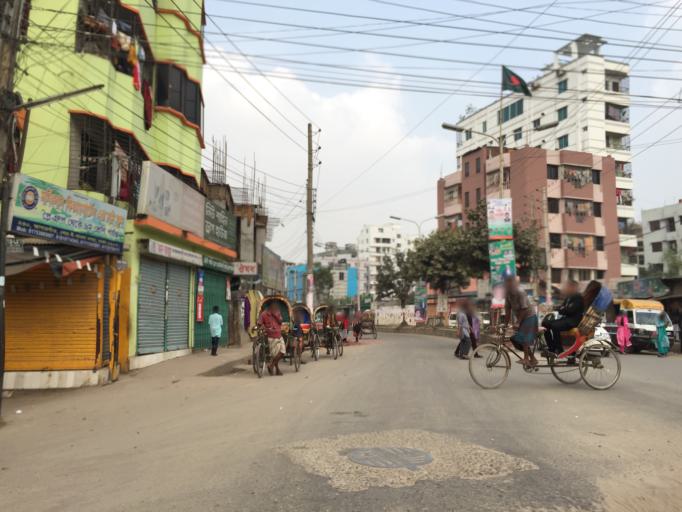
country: BD
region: Dhaka
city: Azimpur
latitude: 23.7805
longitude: 90.3683
